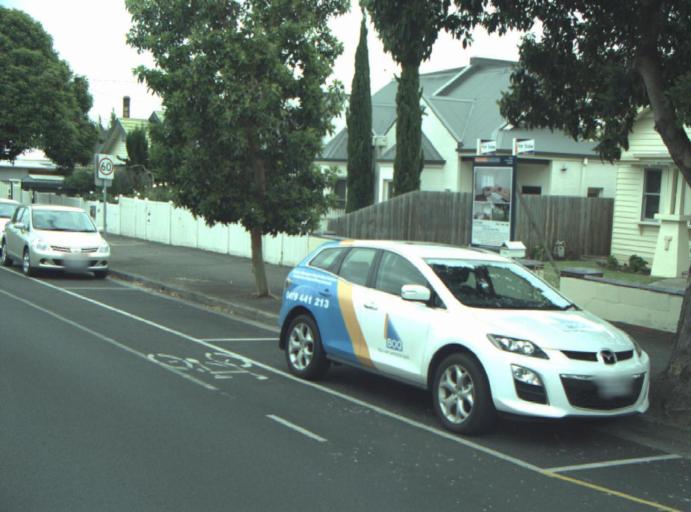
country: AU
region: Victoria
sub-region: Greater Geelong
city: Geelong
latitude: -38.1588
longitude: 144.3449
